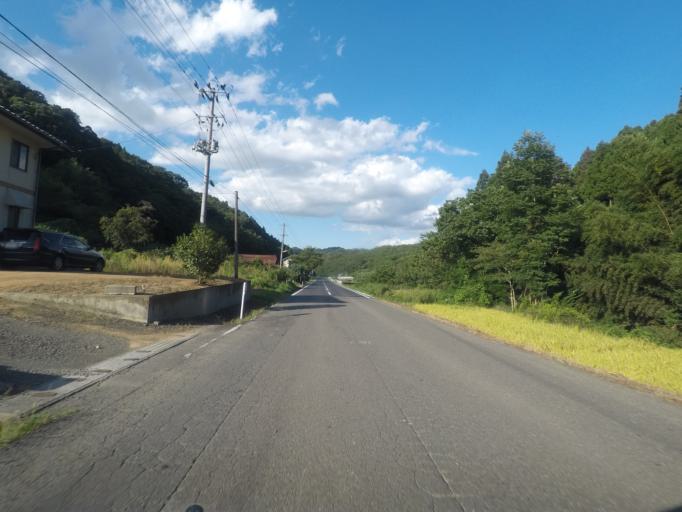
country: JP
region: Fukushima
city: Hobaramachi
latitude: 37.7495
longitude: 140.5581
